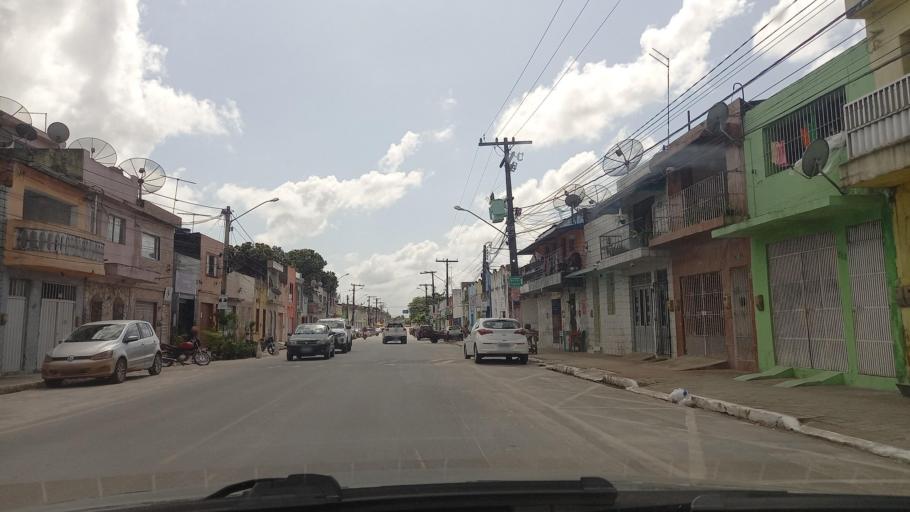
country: BR
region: Pernambuco
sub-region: Goiana
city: Goiana
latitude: -7.5598
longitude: -34.9943
